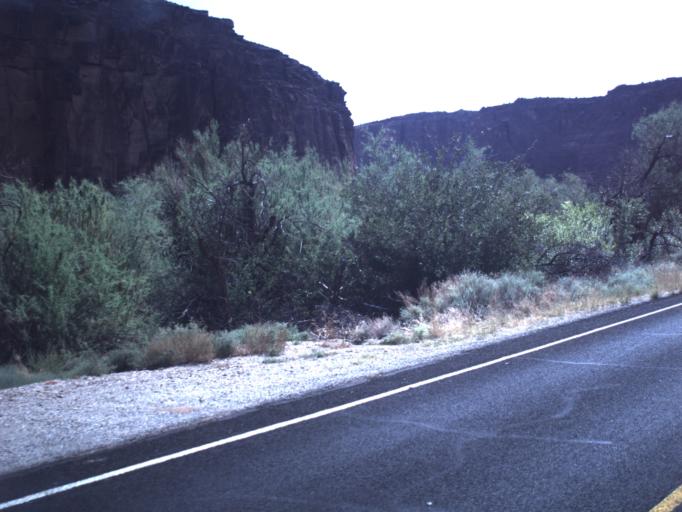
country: US
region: Utah
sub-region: Grand County
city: Moab
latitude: 38.5734
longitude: -109.6538
